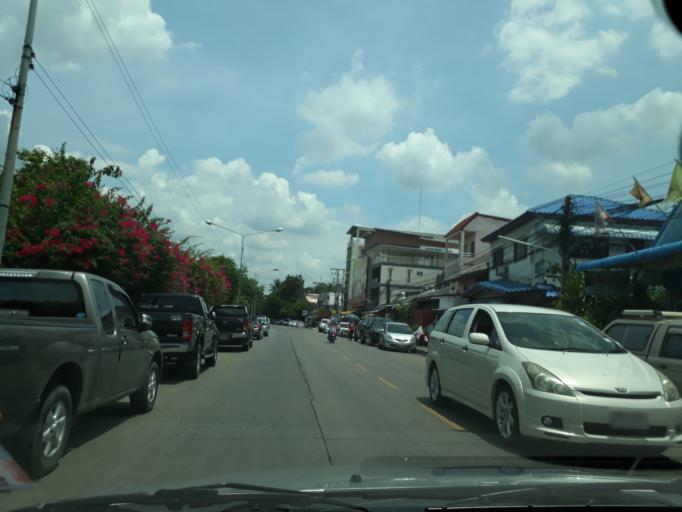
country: TH
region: Khon Kaen
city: Khon Kaen
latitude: 16.4117
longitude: 102.8351
